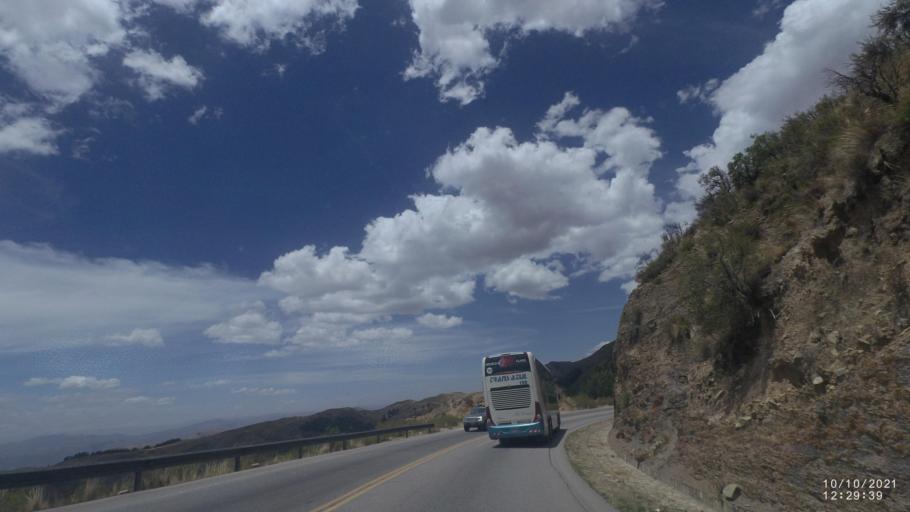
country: BO
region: Cochabamba
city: Irpa Irpa
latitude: -17.6696
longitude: -66.4362
